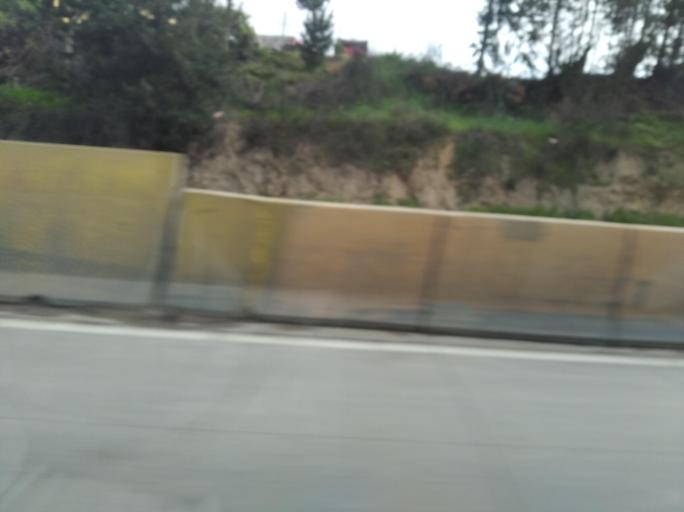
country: CL
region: Valparaiso
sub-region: Provincia de Valparaiso
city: Vina del Mar
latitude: -33.0992
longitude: -71.5726
